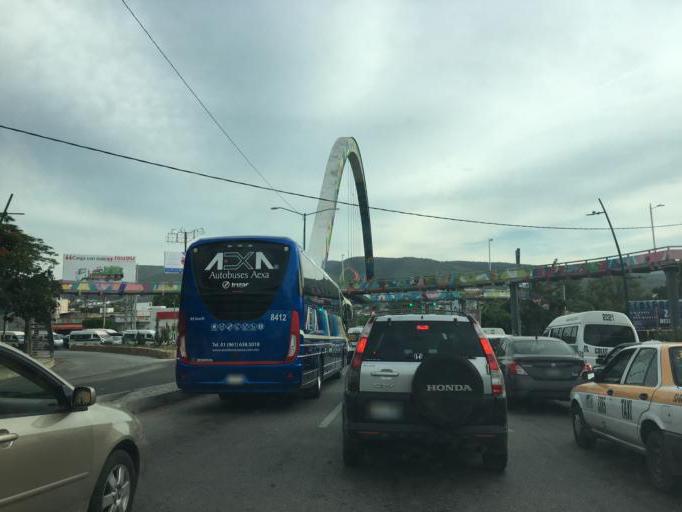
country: MX
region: Chiapas
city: Tuxtla Gutierrez
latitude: 16.7543
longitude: -93.1421
